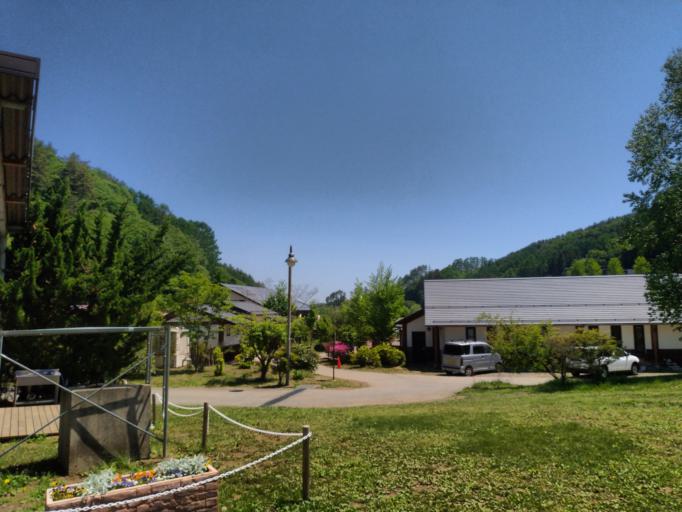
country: JP
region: Yamanashi
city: Nirasaki
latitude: 35.8663
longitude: 138.4280
